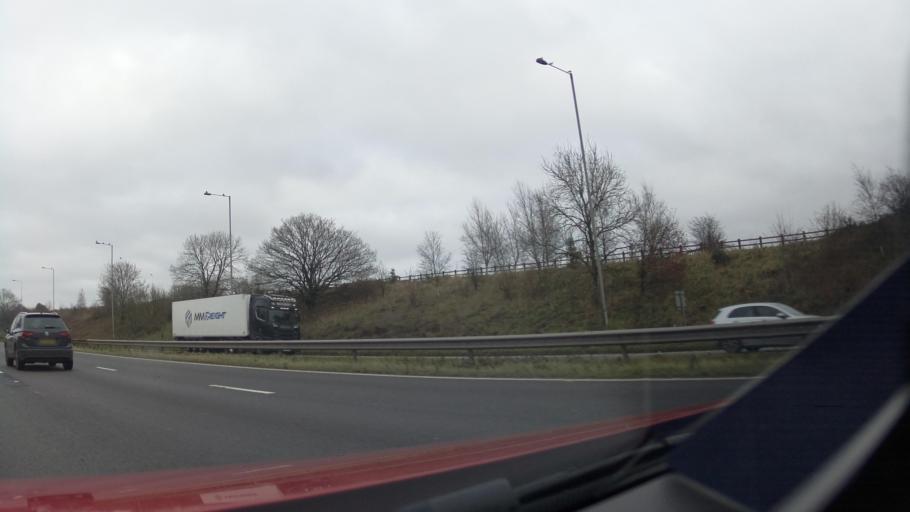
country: GB
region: England
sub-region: Lancashire
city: Euxton
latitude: 53.6714
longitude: -2.6862
